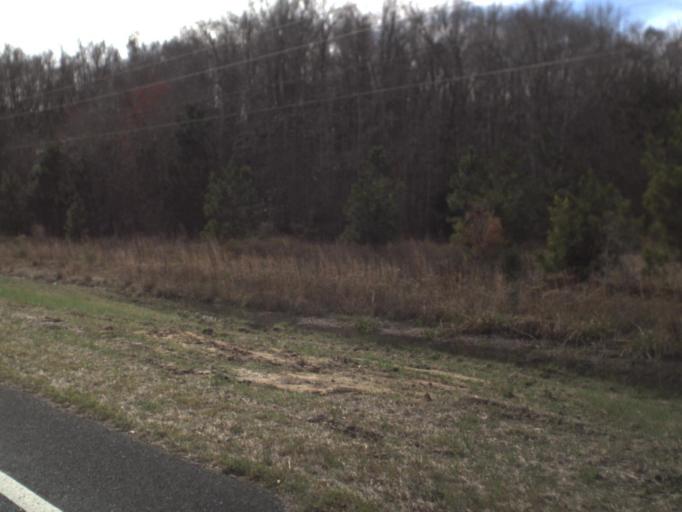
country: US
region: Florida
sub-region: Jackson County
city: Marianna
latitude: 30.7644
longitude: -85.3767
